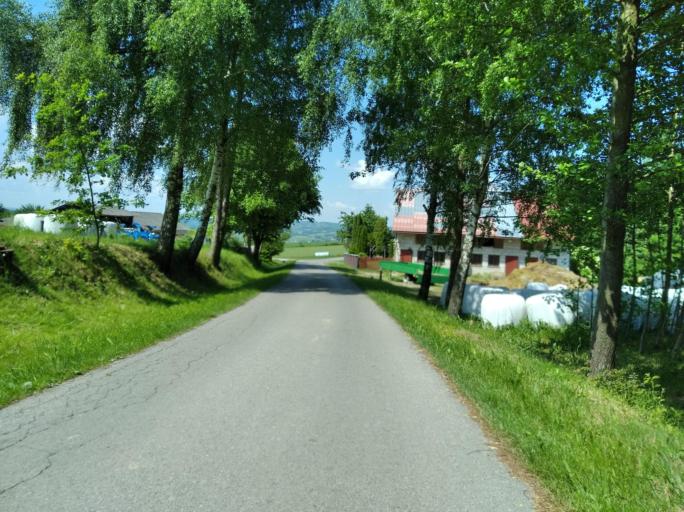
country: PL
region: Subcarpathian Voivodeship
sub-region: Powiat ropczycko-sedziszowski
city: Wielopole Skrzynskie
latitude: 49.9843
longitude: 21.6131
